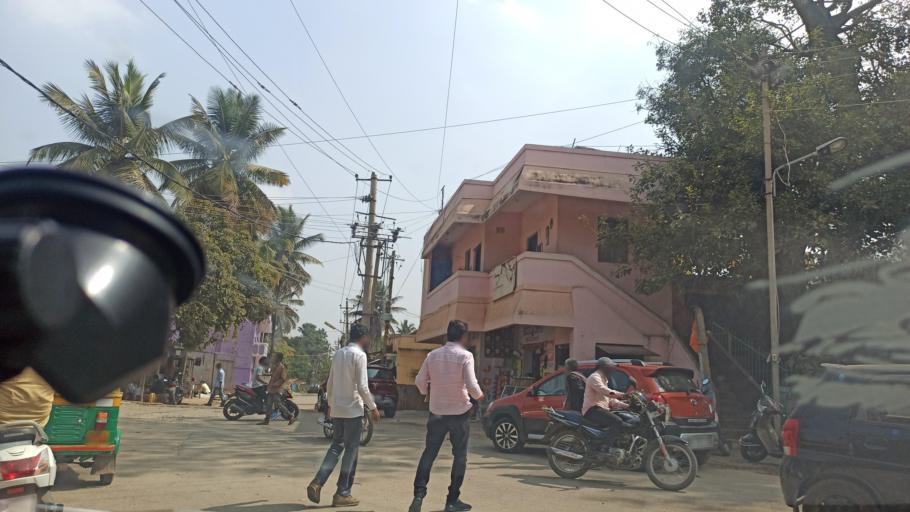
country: IN
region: Karnataka
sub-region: Bangalore Urban
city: Yelahanka
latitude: 13.0794
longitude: 77.6074
